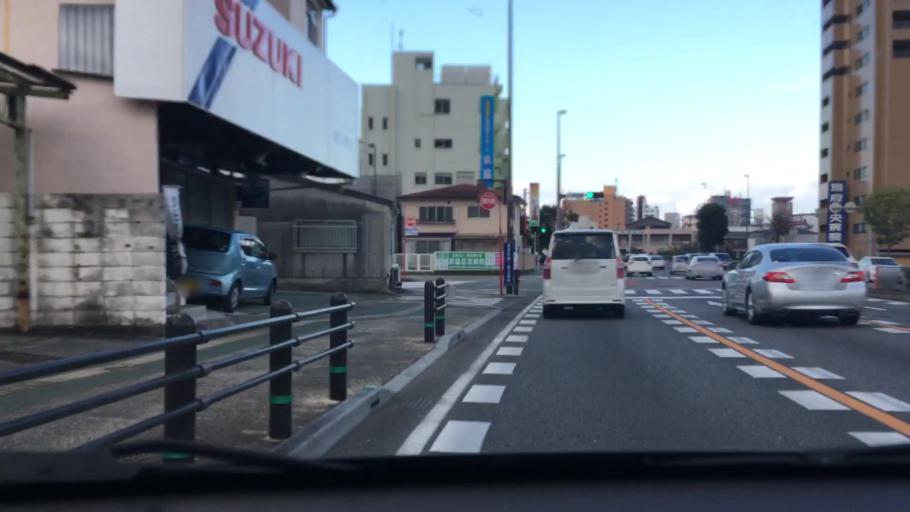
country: JP
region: Oita
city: Beppu
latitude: 33.2696
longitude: 131.5098
